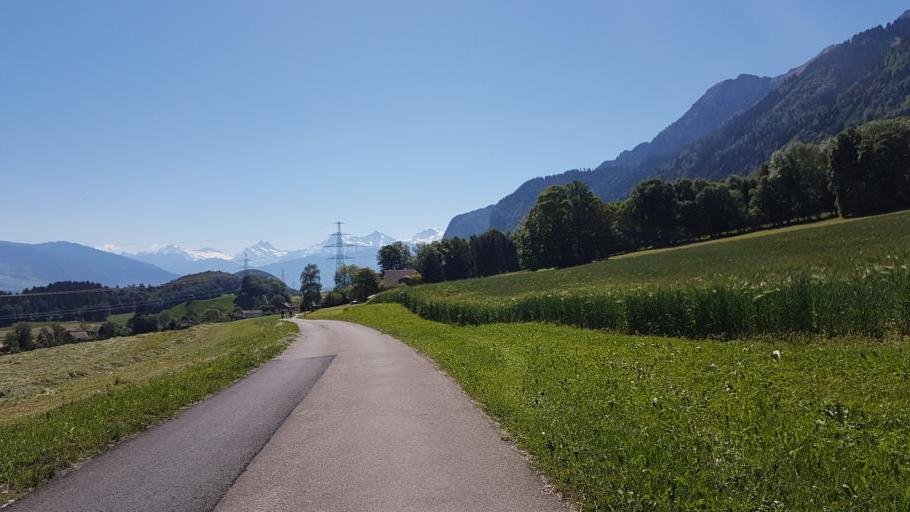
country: CH
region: Bern
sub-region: Thun District
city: Blumenstein
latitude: 46.7253
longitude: 7.5313
